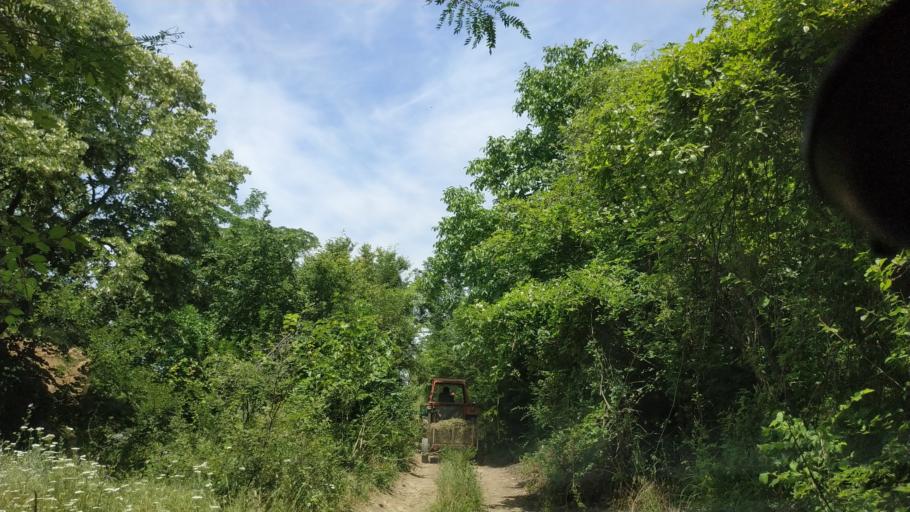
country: RS
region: Central Serbia
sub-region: Nisavski Okrug
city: Aleksinac
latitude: 43.5750
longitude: 21.7040
